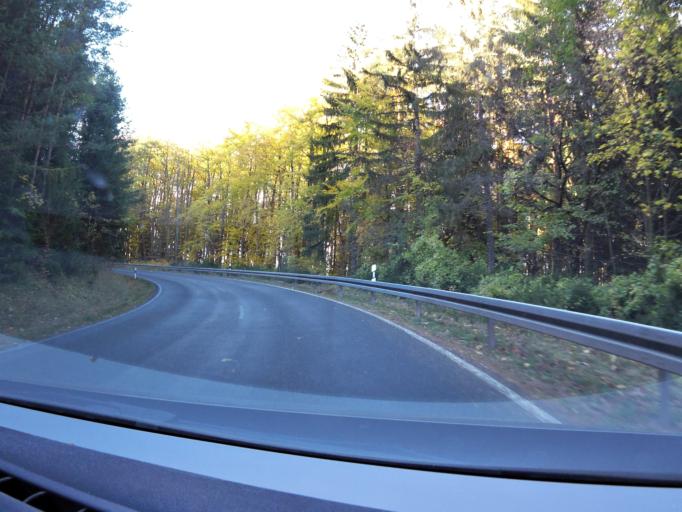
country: DE
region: Thuringia
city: Elgersburg
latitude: 50.7067
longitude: 10.8429
